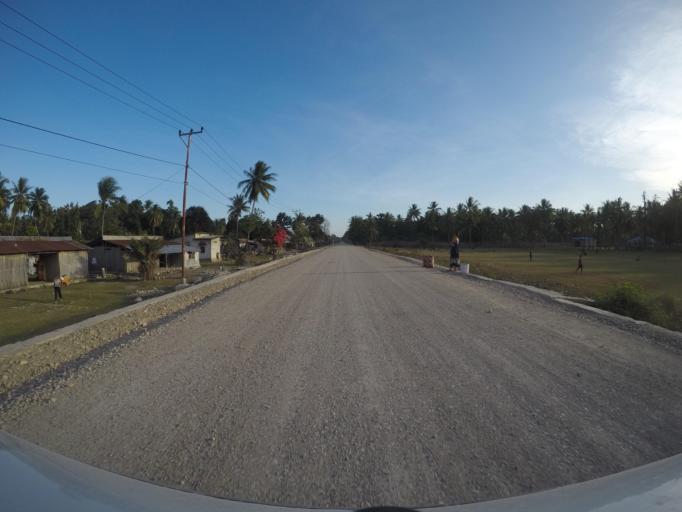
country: TL
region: Viqueque
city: Viqueque
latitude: -8.8502
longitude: 126.5128
